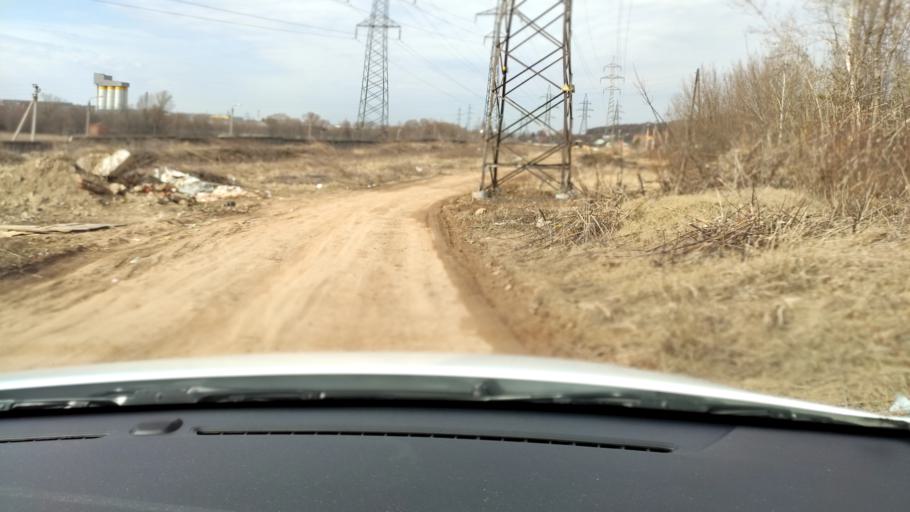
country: RU
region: Tatarstan
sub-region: Gorod Kazan'
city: Kazan
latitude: 55.8173
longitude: 49.2114
